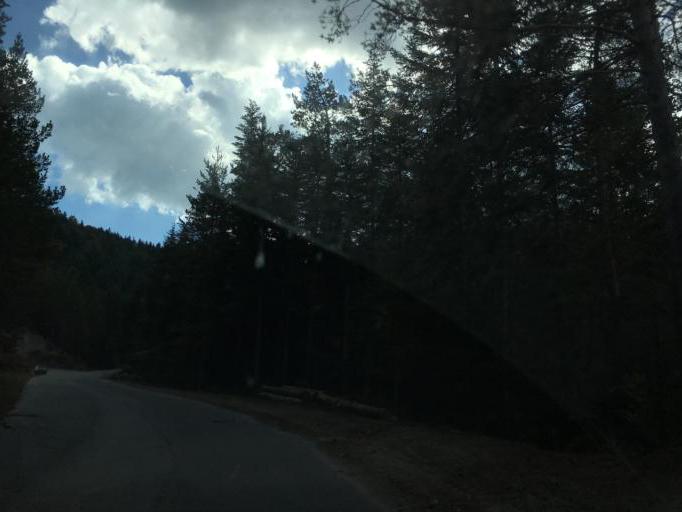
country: BG
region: Pazardzhik
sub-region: Obshtina Batak
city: Batak
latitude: 41.9217
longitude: 24.2833
